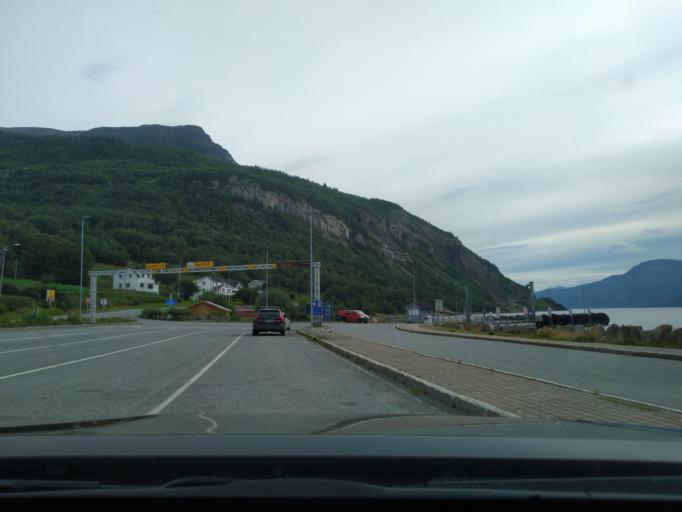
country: NO
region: Nordland
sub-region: Evenes
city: Randa
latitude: 68.7264
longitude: 16.8487
